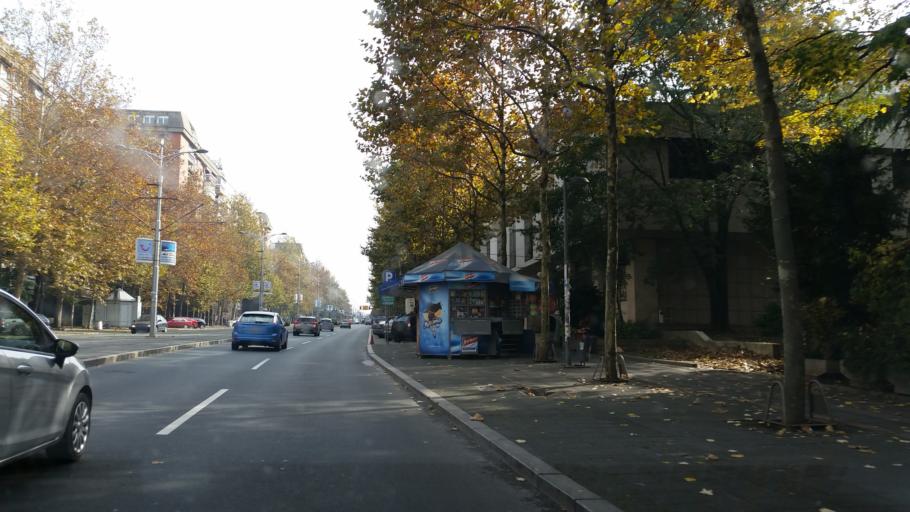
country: RS
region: Central Serbia
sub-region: Belgrade
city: Vracar
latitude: 44.7968
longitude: 20.4958
